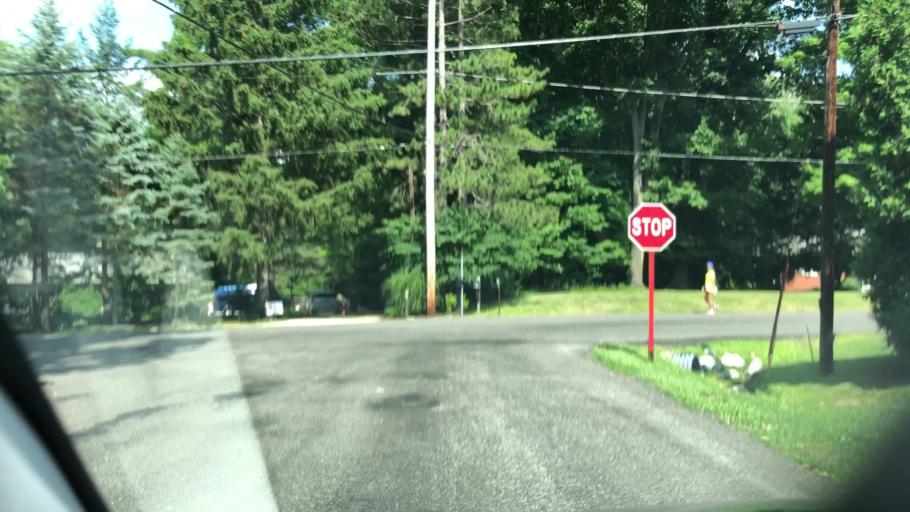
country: US
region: Ohio
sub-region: Summit County
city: Montrose-Ghent
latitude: 41.1582
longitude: -81.6483
